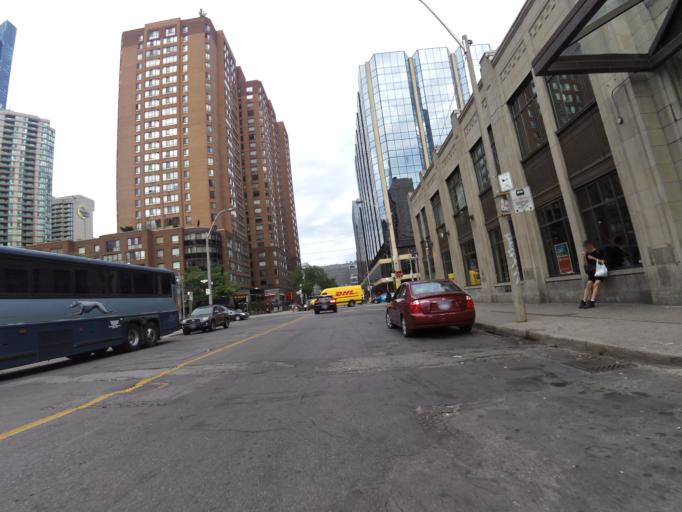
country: CA
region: Ontario
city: Toronto
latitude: 43.6563
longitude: -79.3846
